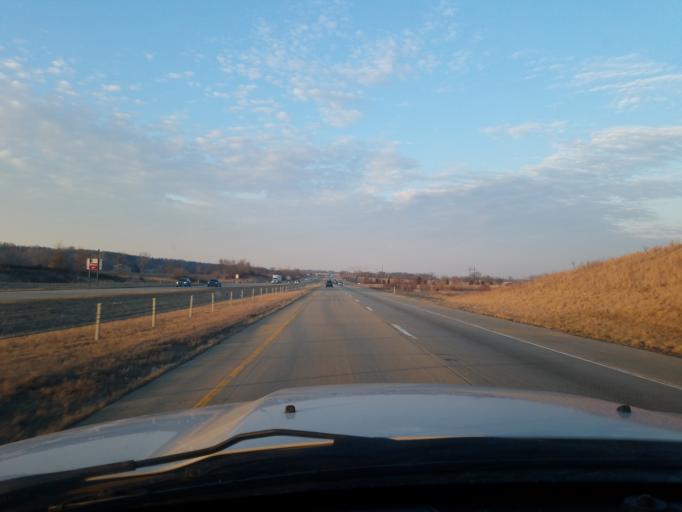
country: US
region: Indiana
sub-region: Vanderburgh County
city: Darmstadt
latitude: 38.1385
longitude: -87.4728
